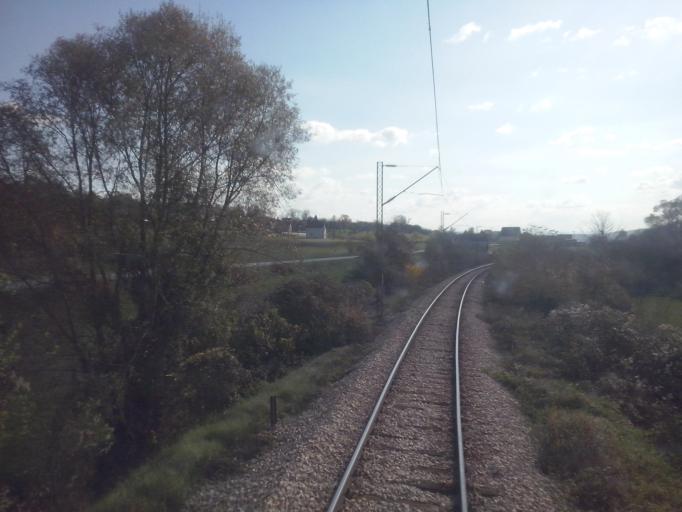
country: RS
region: Central Serbia
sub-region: Zlatiborski Okrug
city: Pozega
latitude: 43.8697
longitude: 20.0083
